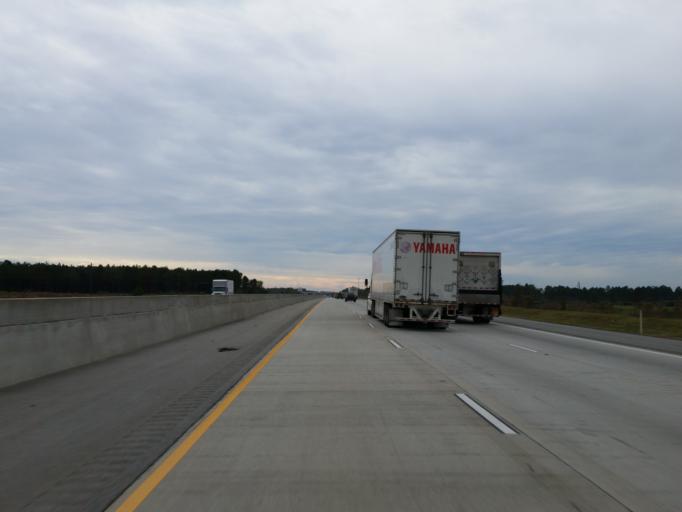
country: US
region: Georgia
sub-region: Tift County
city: Unionville
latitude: 31.3452
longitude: -83.4868
